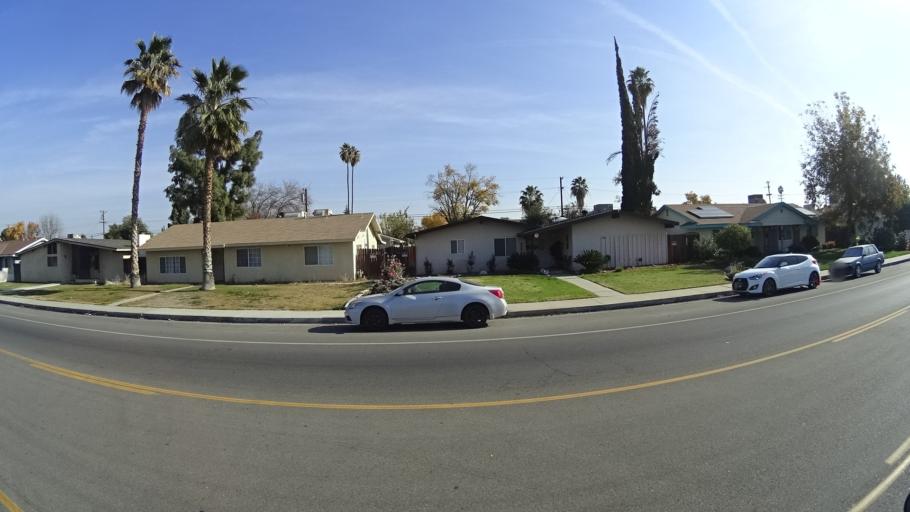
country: US
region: California
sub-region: Kern County
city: Bakersfield
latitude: 35.3259
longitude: -119.0301
